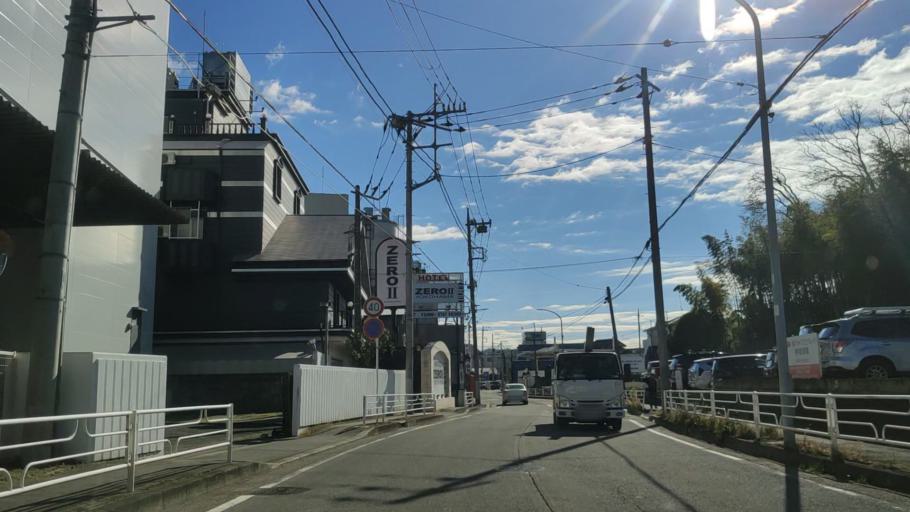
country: JP
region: Kanagawa
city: Yokohama
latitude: 35.4986
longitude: 139.6008
